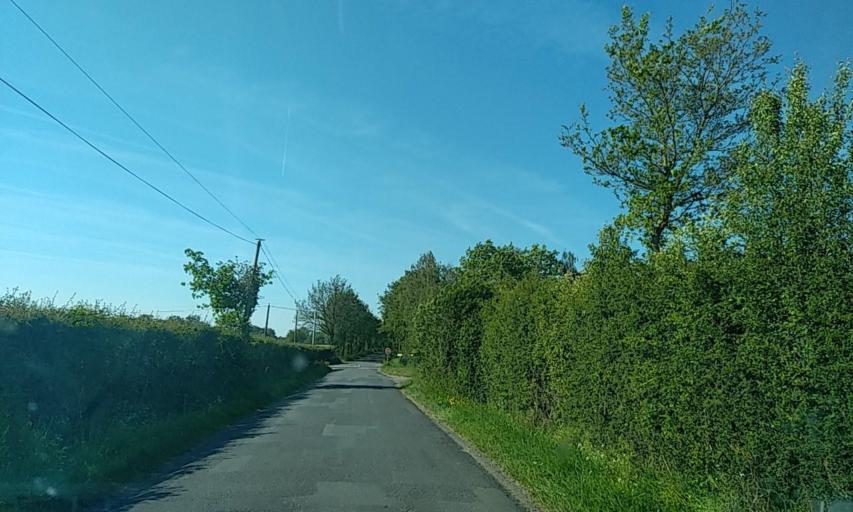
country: FR
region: Poitou-Charentes
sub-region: Departement des Deux-Sevres
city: Boisme
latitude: 46.8101
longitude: -0.4511
